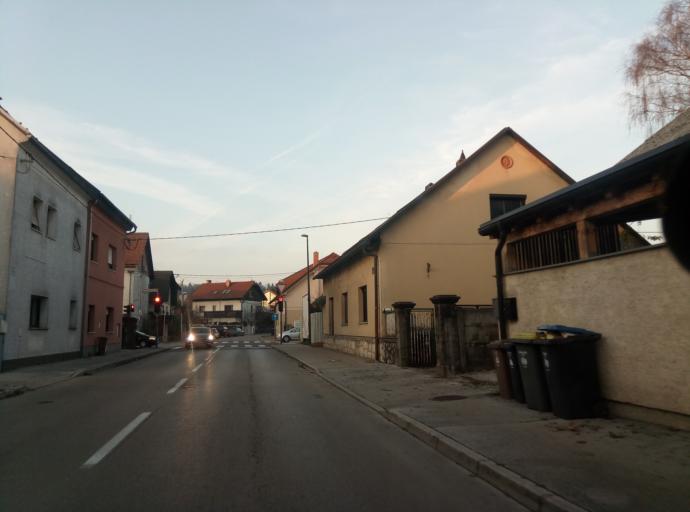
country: SI
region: Ljubljana
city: Ljubljana
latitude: 46.0483
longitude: 14.4854
